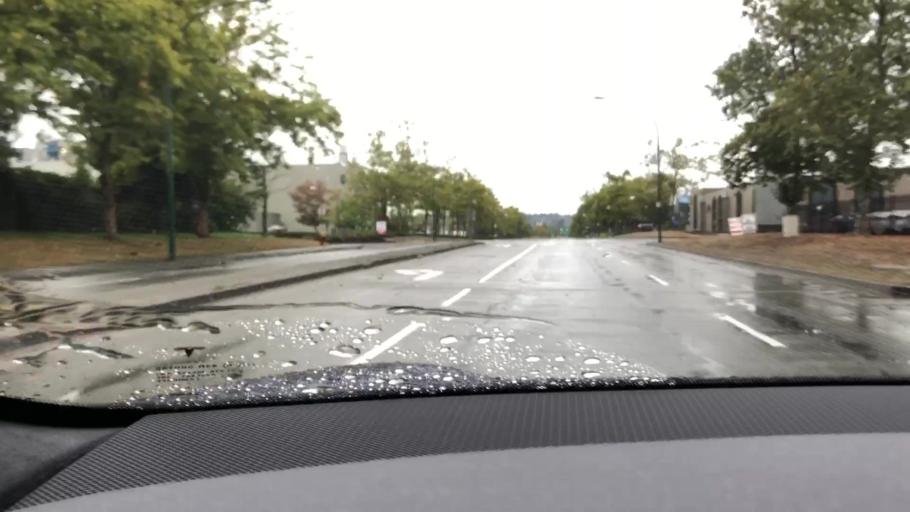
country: CA
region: British Columbia
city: Port Moody
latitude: 49.2283
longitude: -122.8433
